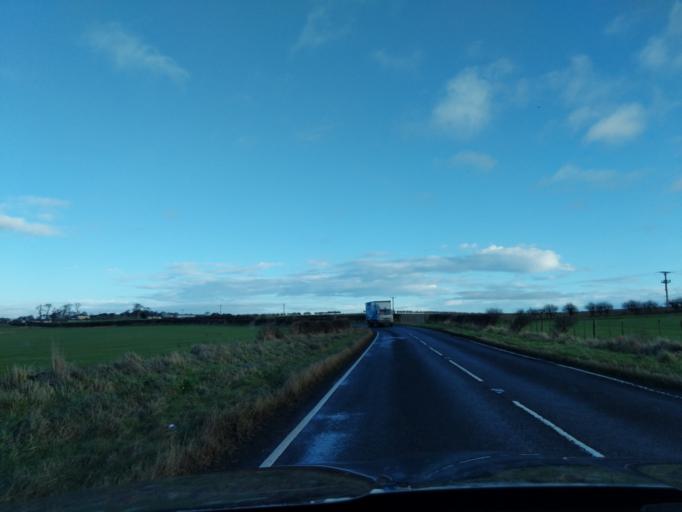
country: GB
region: England
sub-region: Northumberland
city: Ancroft
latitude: 55.7352
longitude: -2.0869
